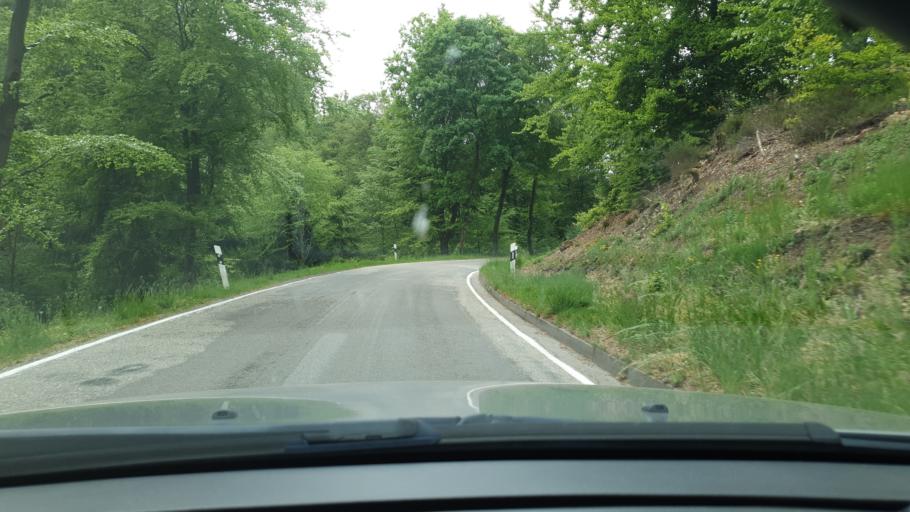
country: DE
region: Rheinland-Pfalz
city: Martinshohe
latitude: 49.3777
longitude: 7.4830
